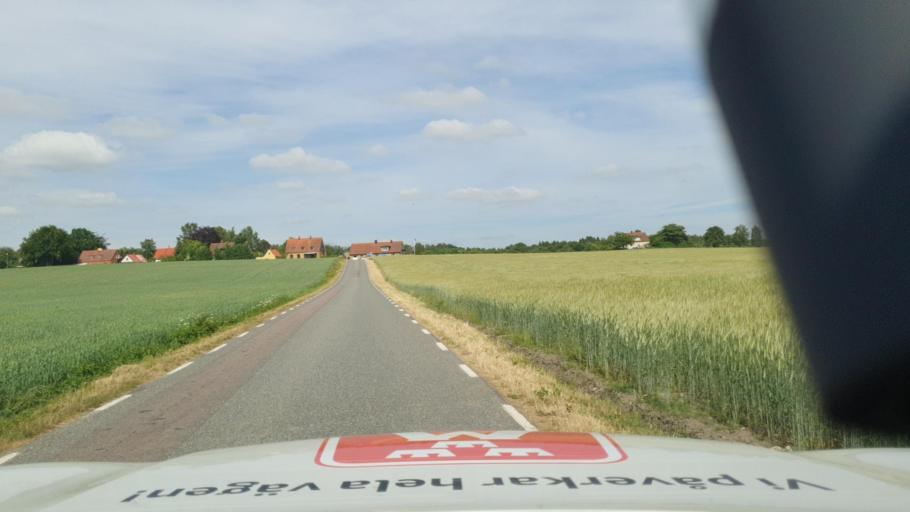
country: SE
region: Skane
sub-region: Tomelilla Kommun
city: Tomelilla
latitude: 55.7151
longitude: 13.9197
